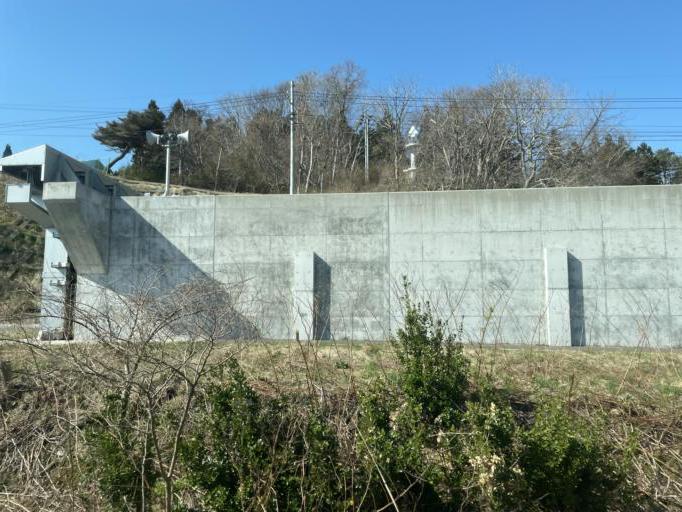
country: JP
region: Aomori
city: Hachinohe
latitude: 40.3464
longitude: 141.7644
